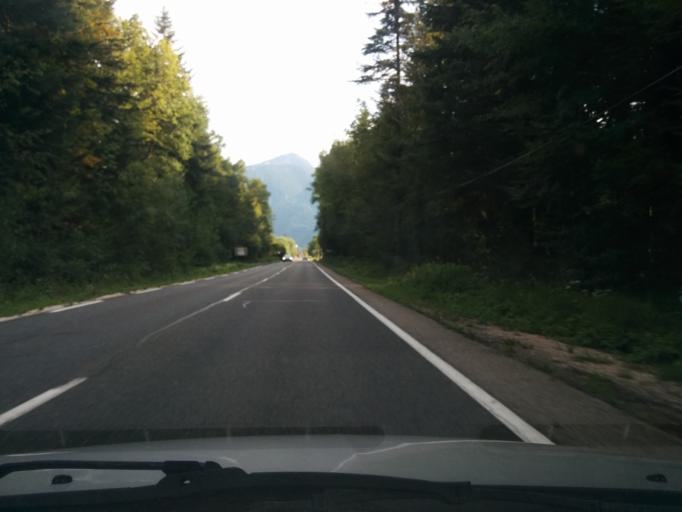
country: FR
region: Rhone-Alpes
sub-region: Departement de l'Isere
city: Entre-deux-Guiers
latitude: 45.4189
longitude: 5.7520
